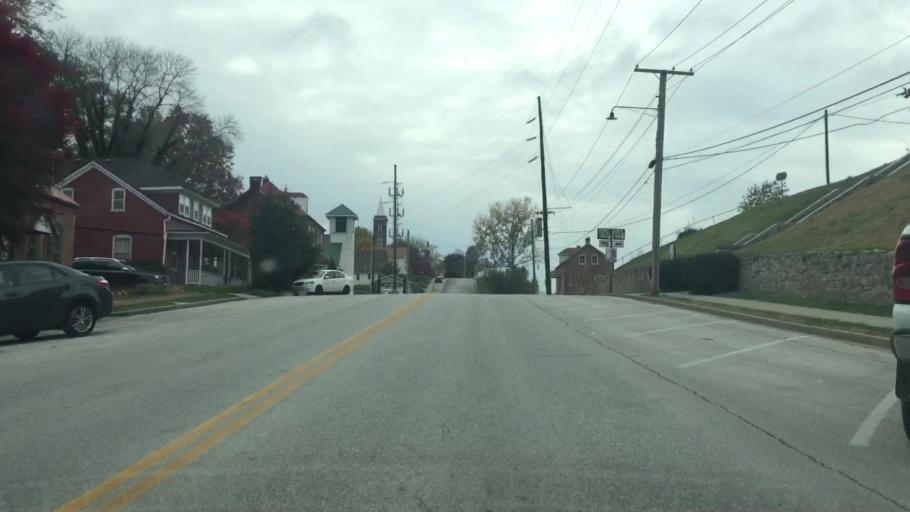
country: US
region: Missouri
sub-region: Gasconade County
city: Hermann
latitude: 38.7069
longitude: -91.4359
